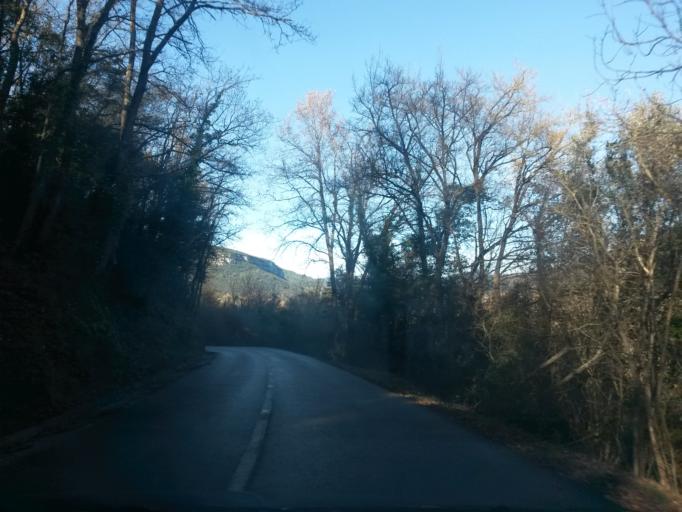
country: ES
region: Catalonia
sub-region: Provincia de Girona
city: la Cellera de Ter
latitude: 42.0253
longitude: 2.6653
